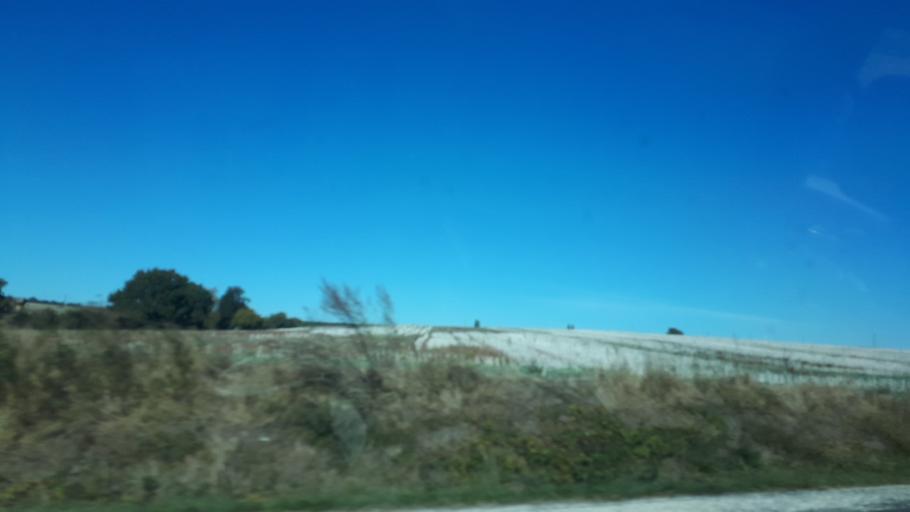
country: FR
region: Centre
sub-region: Departement du Loir-et-Cher
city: Moree
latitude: 47.9417
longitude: 1.2068
